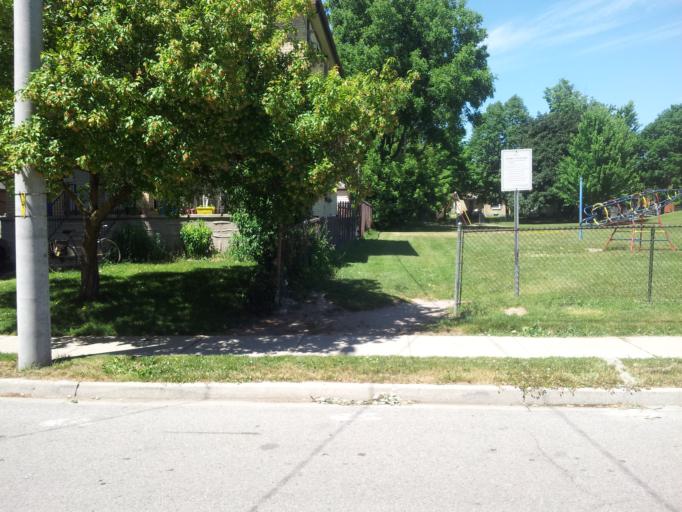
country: CA
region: Ontario
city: Stratford
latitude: 43.3696
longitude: -80.9743
